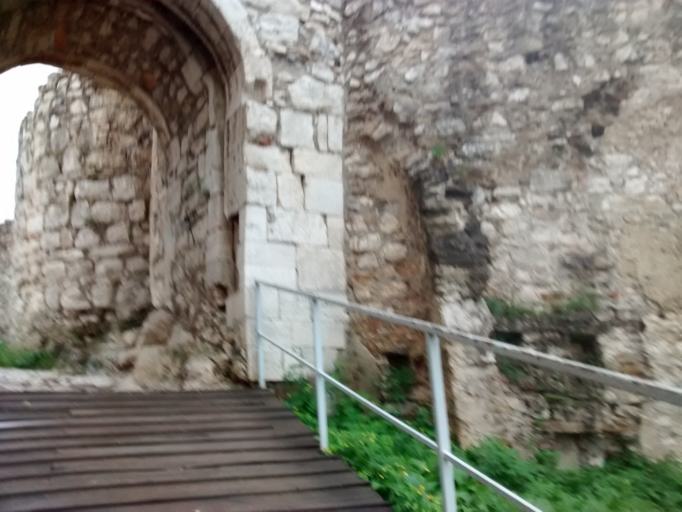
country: SK
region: Presovsky
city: Spisske Podhradie
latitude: 49.0000
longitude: 20.7685
